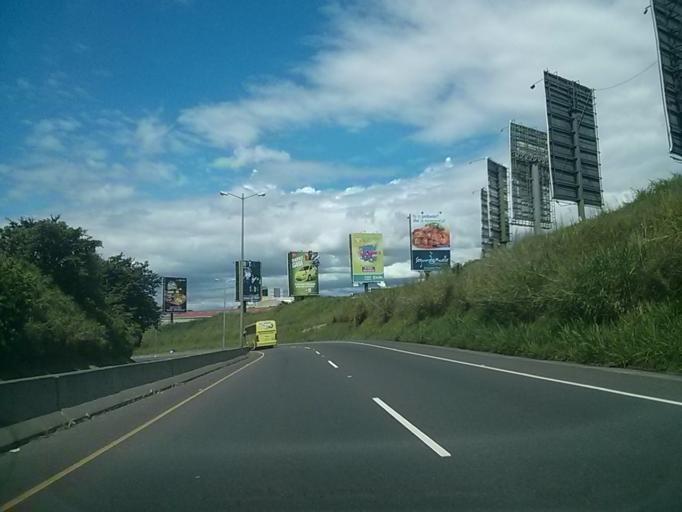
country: CR
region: San Jose
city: San Rafael
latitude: 9.9353
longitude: -84.1129
